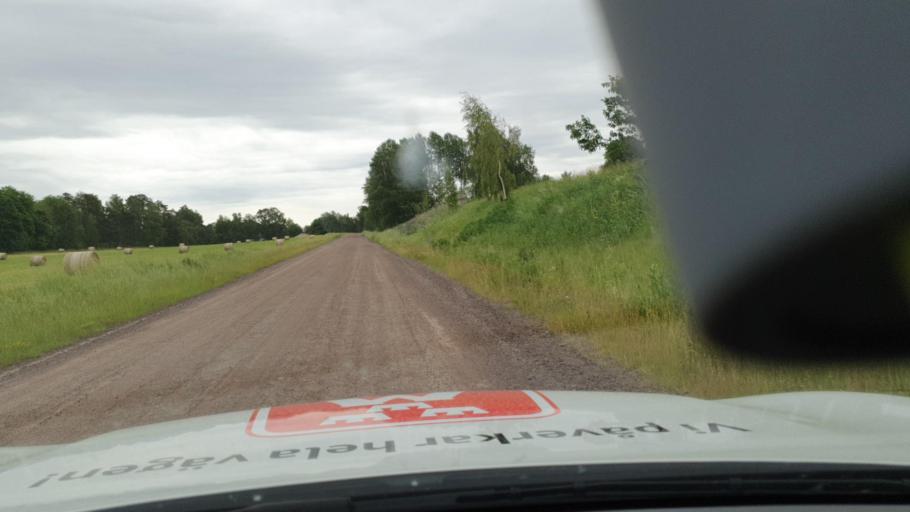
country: SE
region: Vaestra Goetaland
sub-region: Skovde Kommun
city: Skoevde
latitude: 58.3721
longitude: 13.8630
